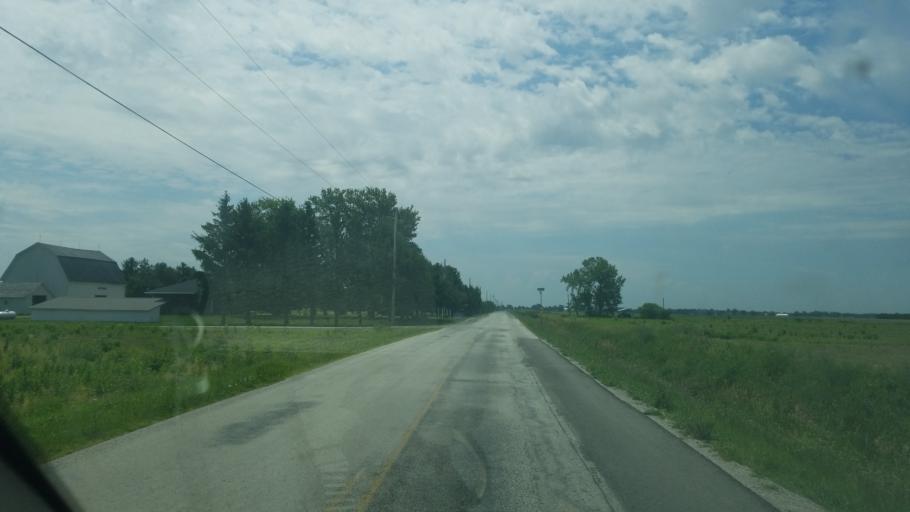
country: US
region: Ohio
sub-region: Wood County
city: Bowling Green
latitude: 41.2900
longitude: -83.5926
